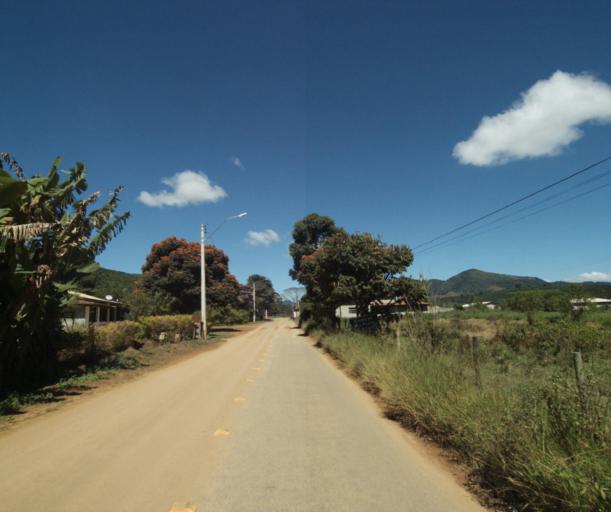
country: BR
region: Minas Gerais
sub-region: Espera Feliz
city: Espera Feliz
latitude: -20.5577
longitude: -41.8204
